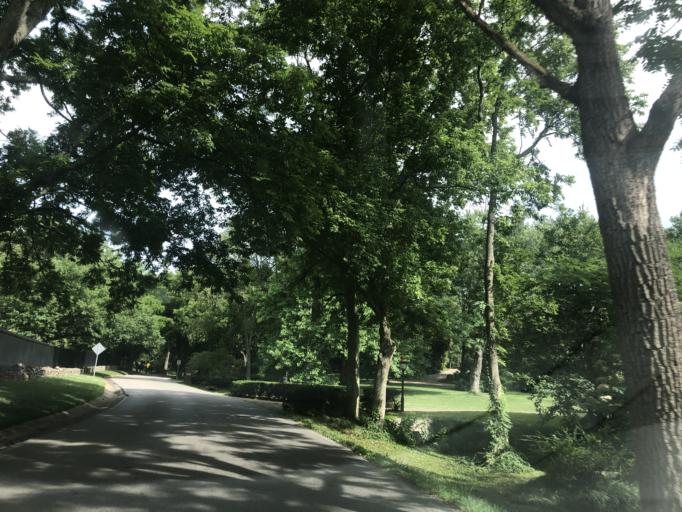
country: US
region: Tennessee
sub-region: Davidson County
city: Oak Hill
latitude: 36.0902
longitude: -86.7772
